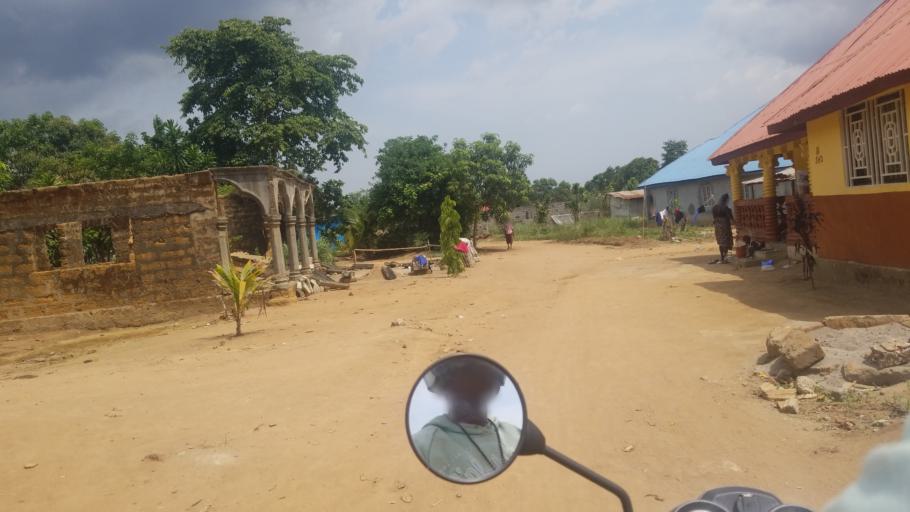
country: SL
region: Western Area
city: Waterloo
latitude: 8.3177
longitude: -13.0466
